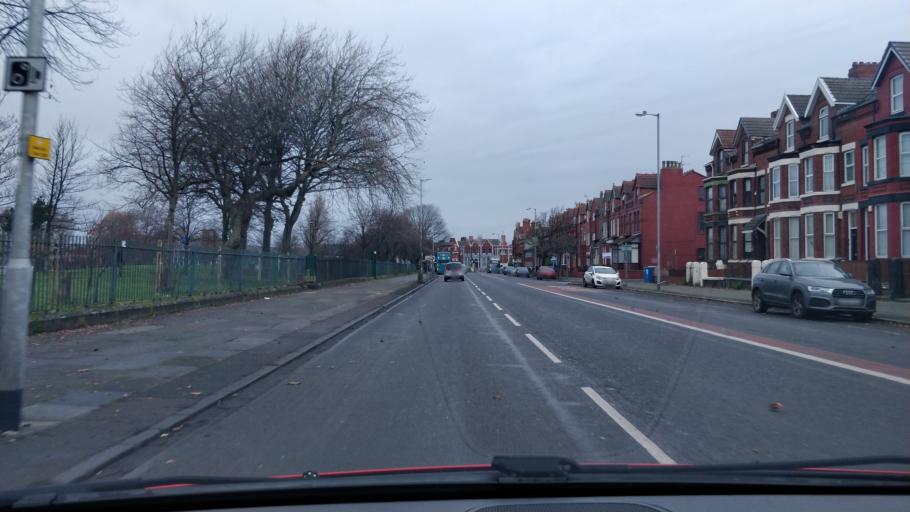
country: GB
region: England
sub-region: Sefton
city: Litherland
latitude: 53.4564
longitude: -2.9919
